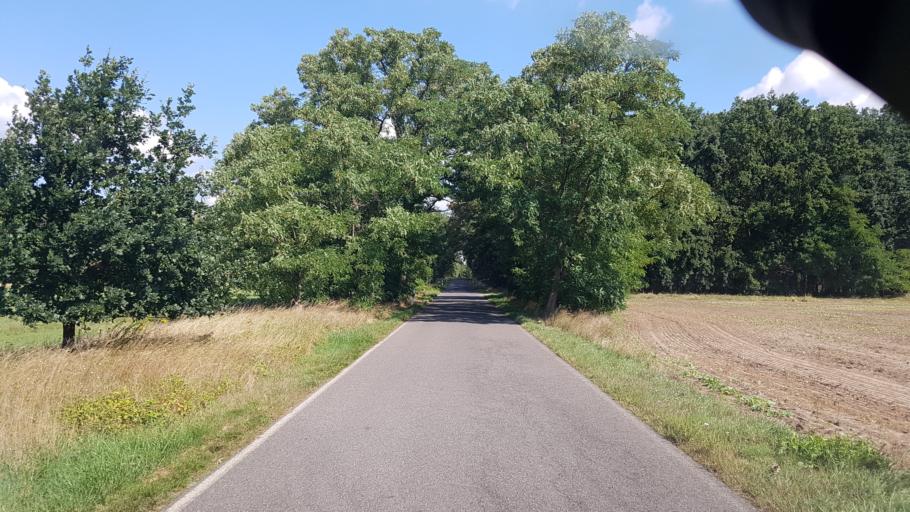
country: DE
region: Brandenburg
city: Drebkau
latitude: 51.6642
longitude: 14.2232
